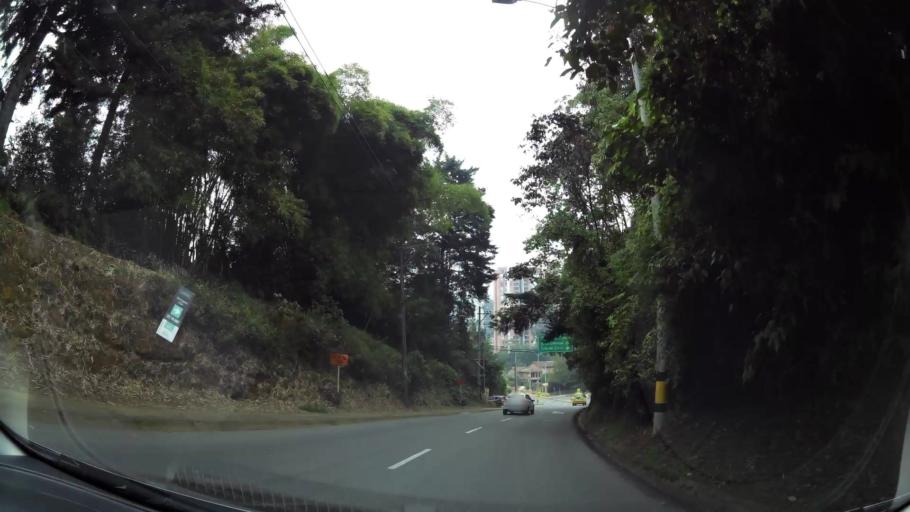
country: CO
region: Antioquia
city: Medellin
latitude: 6.2060
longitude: -75.5553
